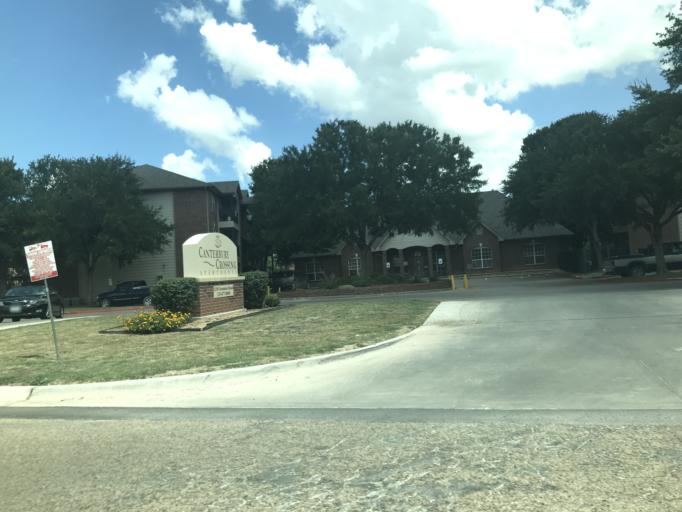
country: US
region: Texas
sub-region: Taylor County
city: Abilene
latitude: 32.4442
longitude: -99.7024
